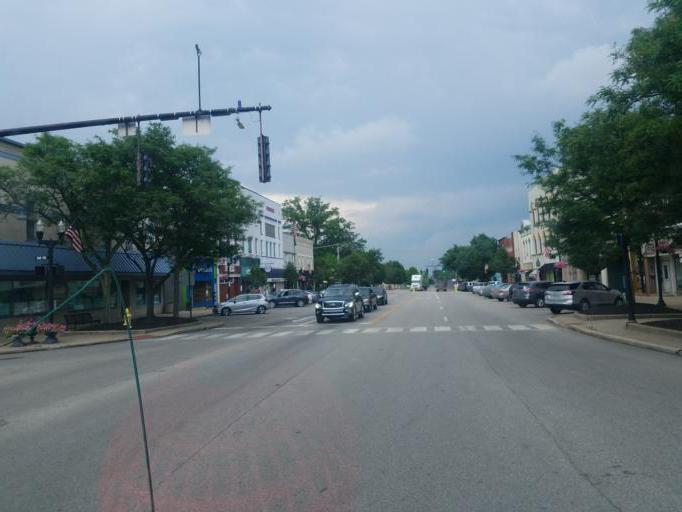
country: US
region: Ohio
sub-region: Medina County
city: Wadsworth
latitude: 41.0255
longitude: -81.7296
